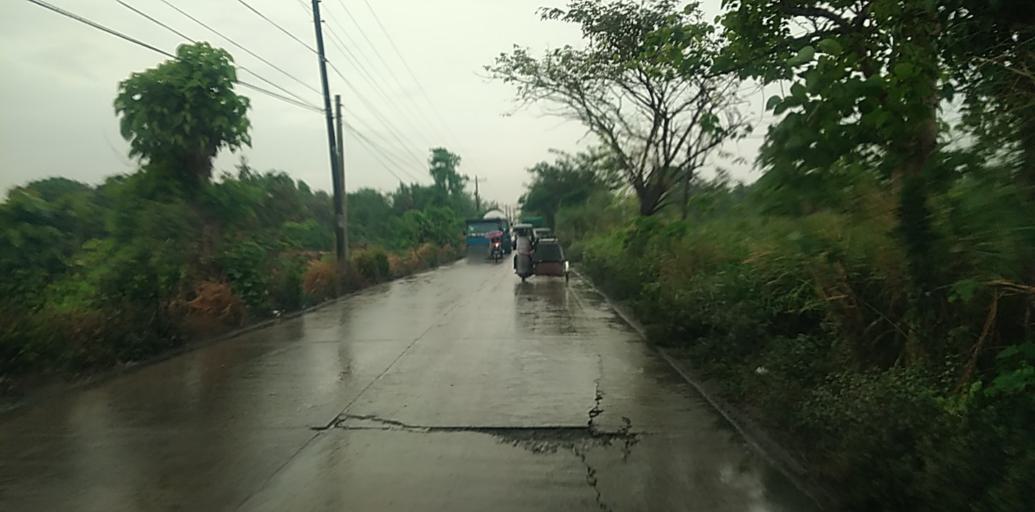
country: PH
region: Central Luzon
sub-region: Province of Pampanga
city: San Antonio
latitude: 15.1489
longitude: 120.6901
